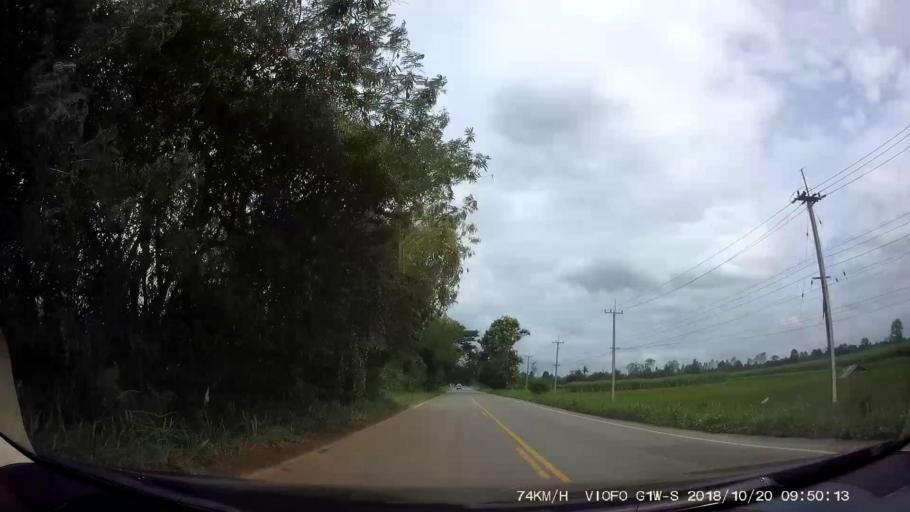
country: TH
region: Chaiyaphum
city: Khon San
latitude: 16.5286
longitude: 101.9028
